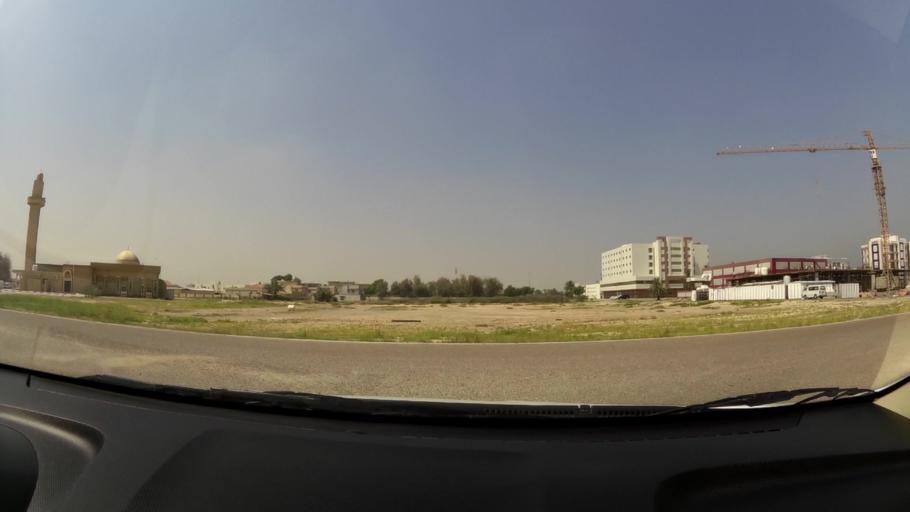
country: AE
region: Umm al Qaywayn
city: Umm al Qaywayn
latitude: 25.5676
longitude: 55.5565
